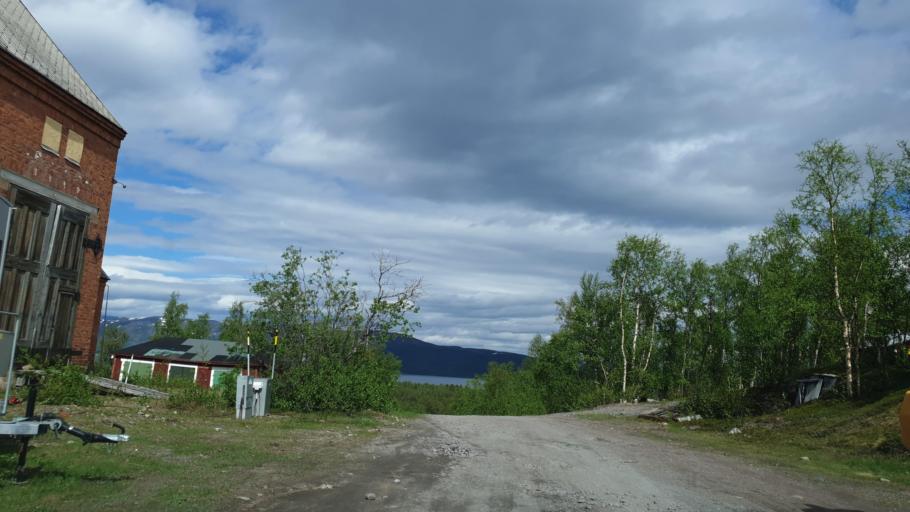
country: SE
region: Norrbotten
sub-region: Kiruna Kommun
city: Kiruna
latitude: 68.2177
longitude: 19.7110
